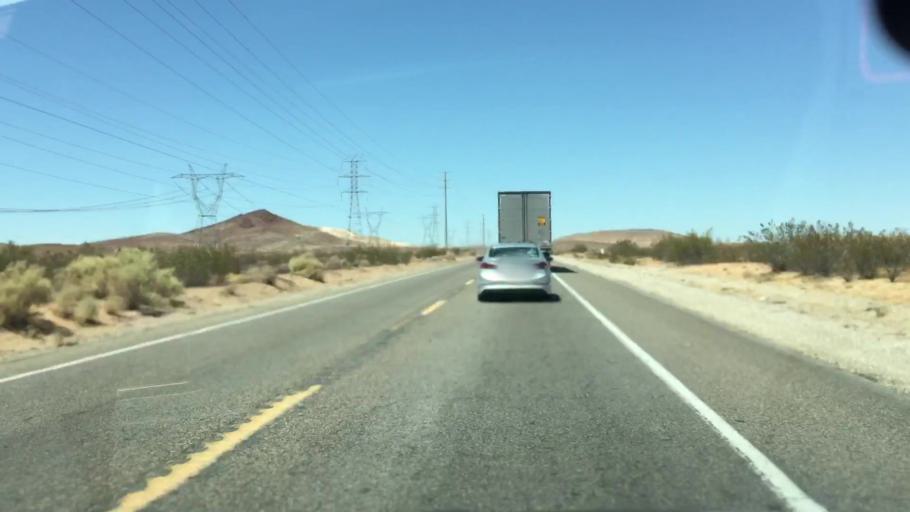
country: US
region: California
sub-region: Kern County
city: Boron
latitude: 34.8541
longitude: -117.5033
